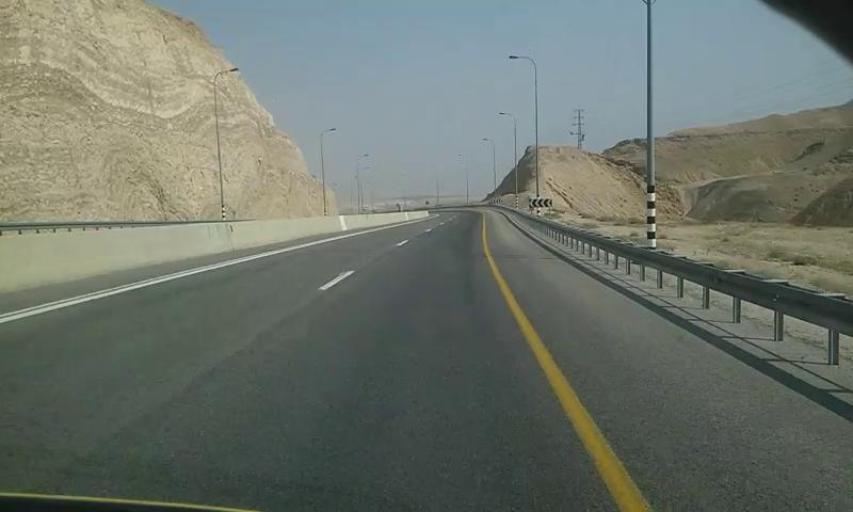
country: PS
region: West Bank
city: Jericho
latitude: 31.7996
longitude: 35.4416
